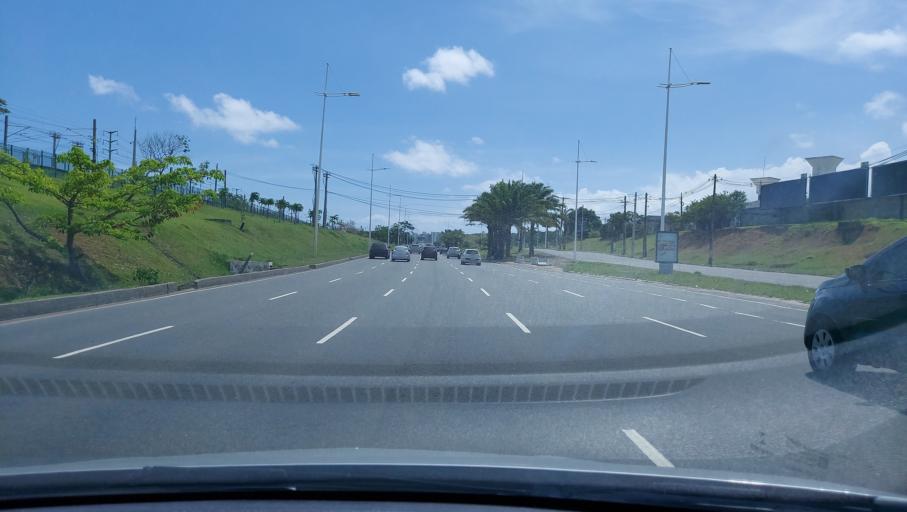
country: BR
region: Bahia
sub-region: Lauro De Freitas
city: Lauro de Freitas
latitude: -12.9273
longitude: -38.3861
